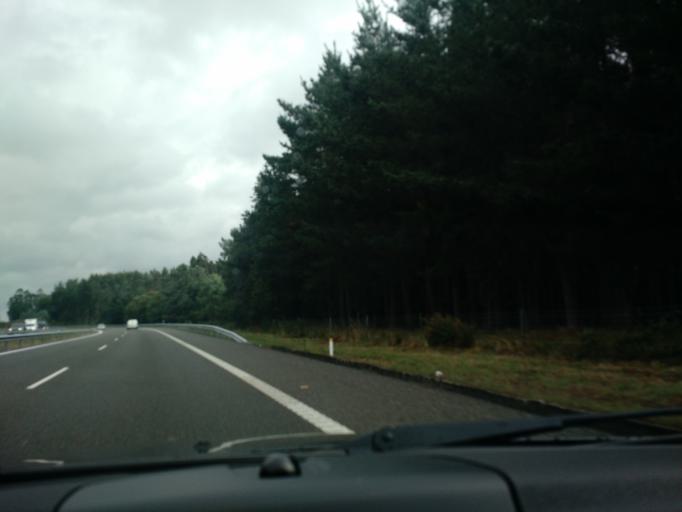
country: ES
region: Galicia
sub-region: Provincia da Coruna
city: Oroso
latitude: 42.9895
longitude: -8.4295
